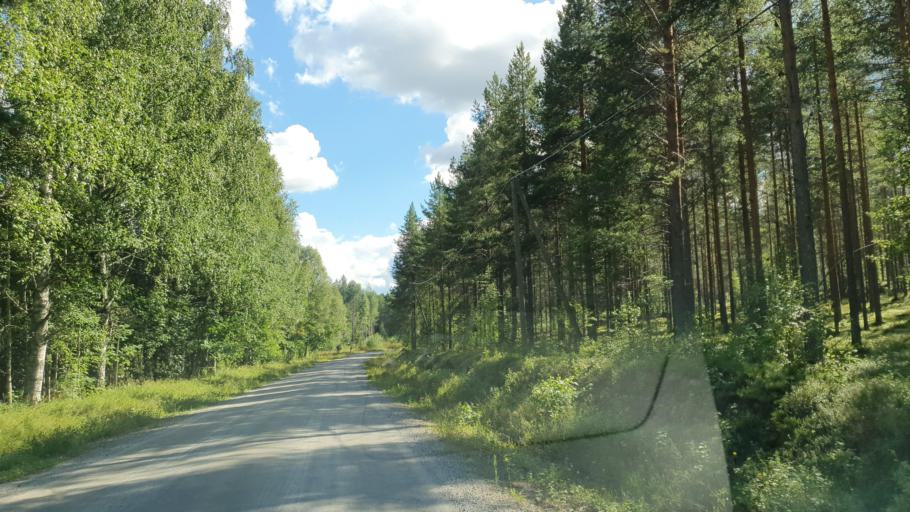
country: FI
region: Kainuu
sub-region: Kehys-Kainuu
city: Kuhmo
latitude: 64.1020
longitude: 29.4026
